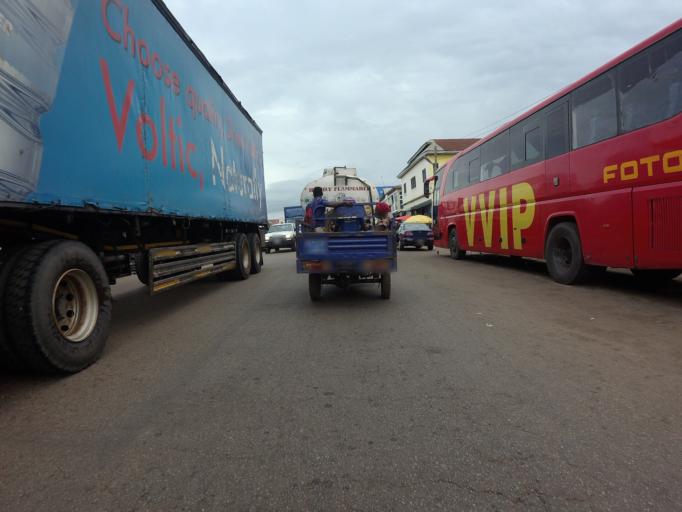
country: GH
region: Ashanti
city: Konongo
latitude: 6.6249
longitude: -1.2100
